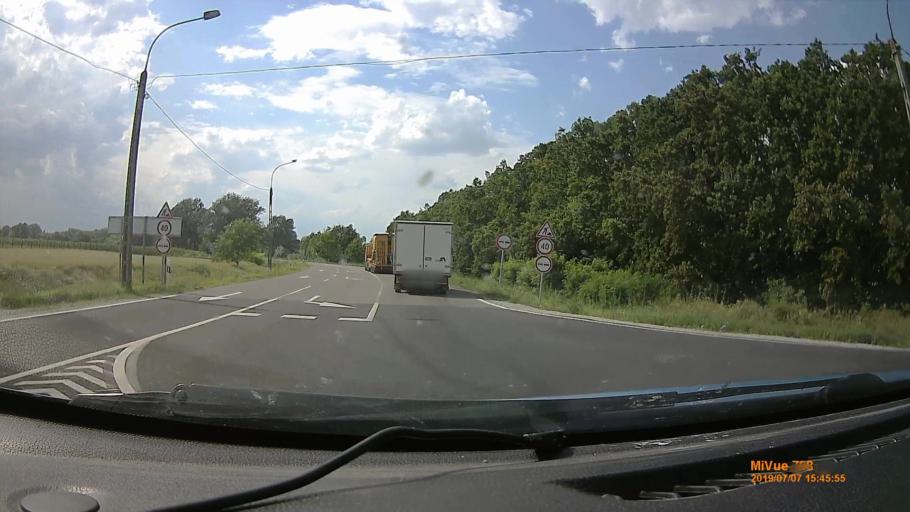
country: HU
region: Jasz-Nagykun-Szolnok
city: Jaszbereny
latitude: 47.5173
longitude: 19.8998
